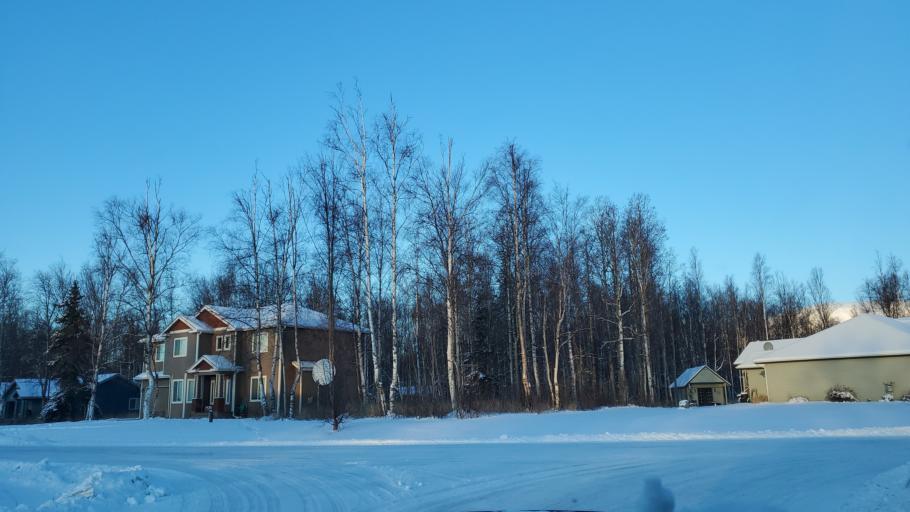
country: US
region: Alaska
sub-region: Matanuska-Susitna Borough
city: Lakes
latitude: 61.6366
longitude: -149.3093
